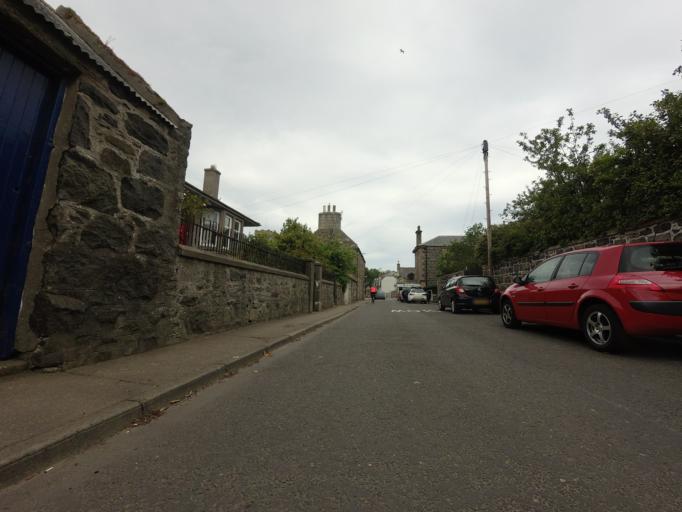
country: GB
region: Scotland
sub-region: Aberdeenshire
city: Portsoy
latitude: 57.6810
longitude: -2.6900
